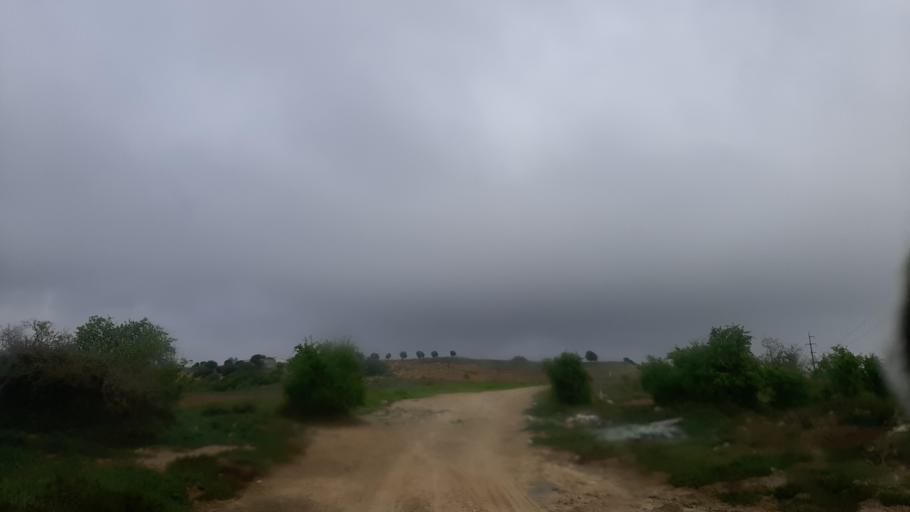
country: TN
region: Nabul
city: Qulaybiyah
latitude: 36.8231
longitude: 11.0476
